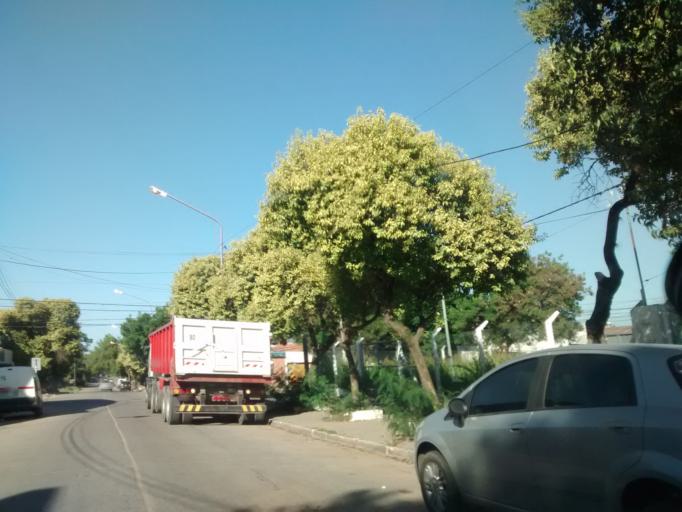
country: AR
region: Chaco
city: Fontana
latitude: -27.4357
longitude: -59.0029
